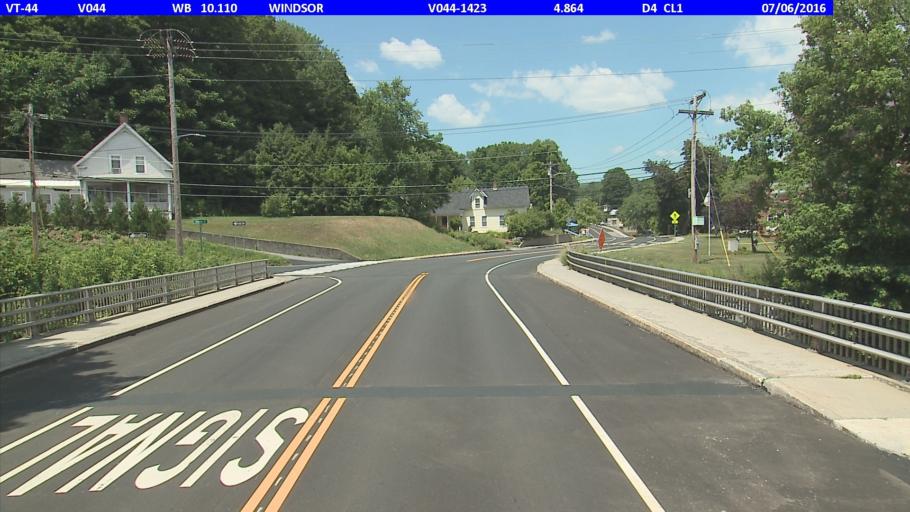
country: US
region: Vermont
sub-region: Windsor County
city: Windsor
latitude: 43.4760
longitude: -72.3899
